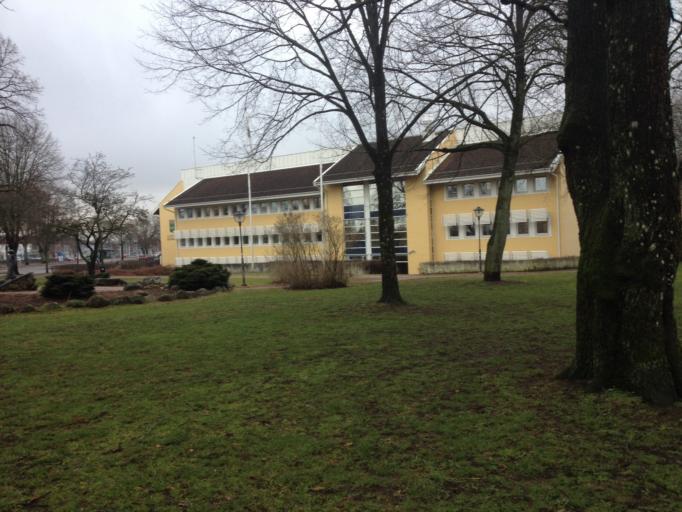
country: SE
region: Kronoberg
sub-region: Ljungby Kommun
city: Ljungby
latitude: 56.8331
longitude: 13.9378
